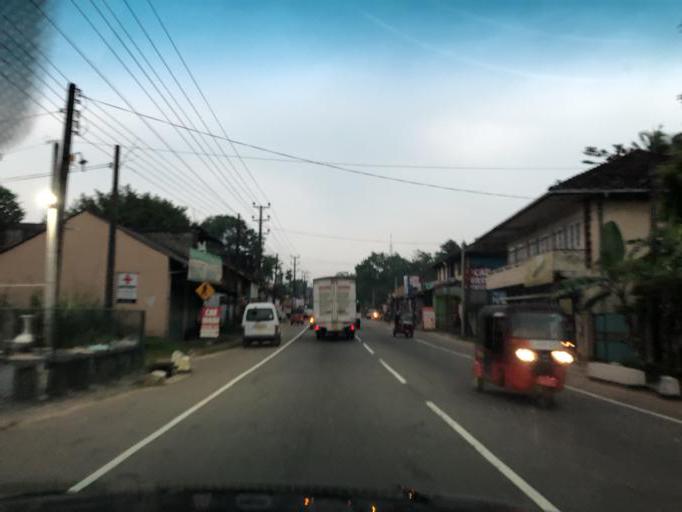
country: LK
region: Western
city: Horana South
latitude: 6.7219
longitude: 80.0762
